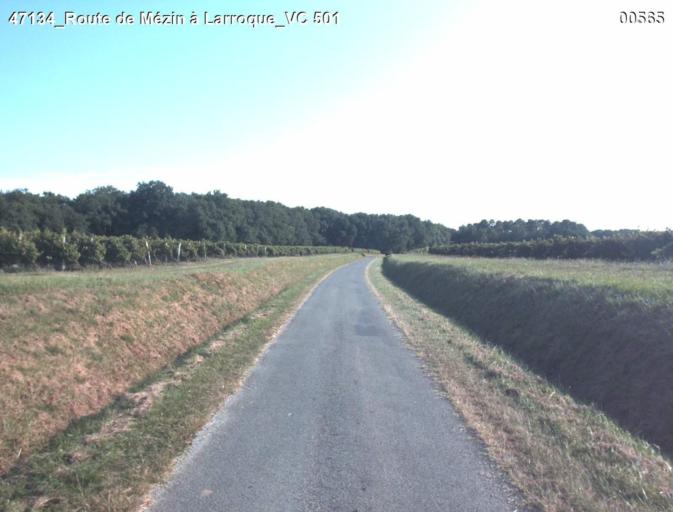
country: FR
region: Aquitaine
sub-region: Departement du Lot-et-Garonne
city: Mezin
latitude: 44.0037
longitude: 0.2784
